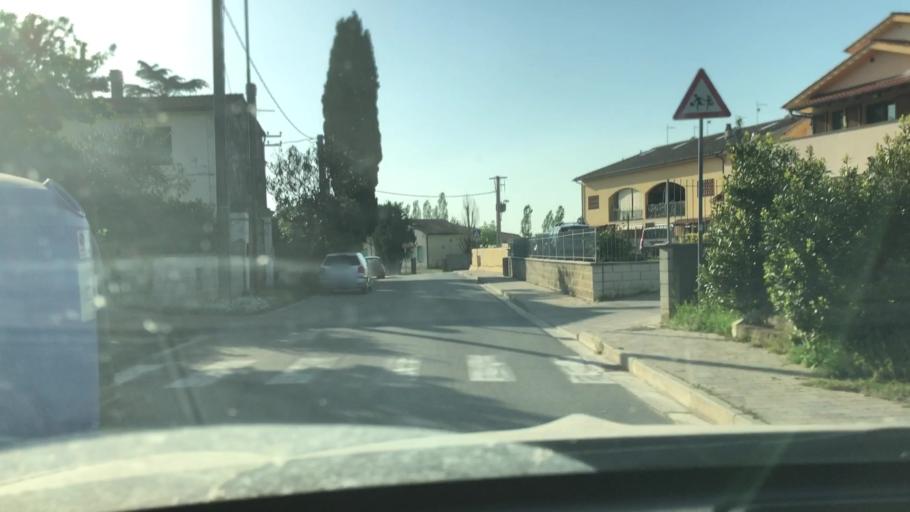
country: IT
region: Tuscany
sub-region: Province of Pisa
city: Cenaia
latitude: 43.5906
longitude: 10.5382
